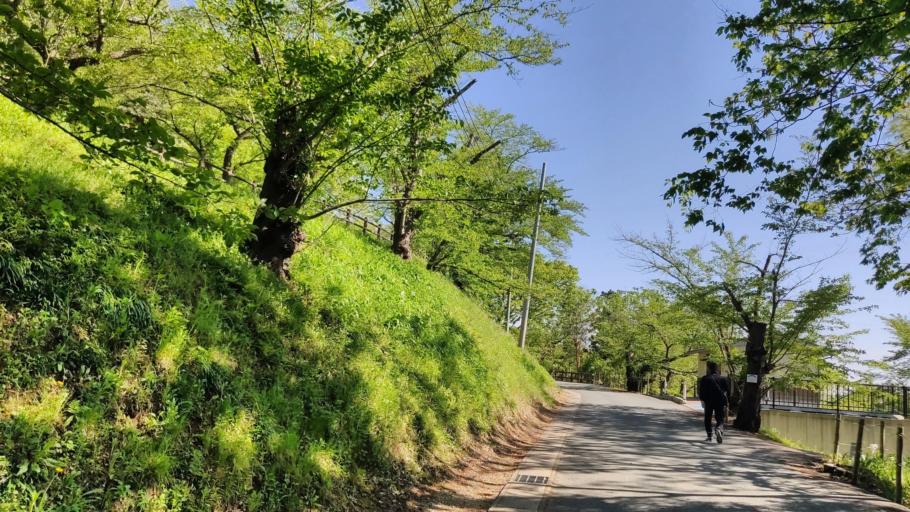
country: JP
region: Yamagata
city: Tendo
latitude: 38.3532
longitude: 140.3738
